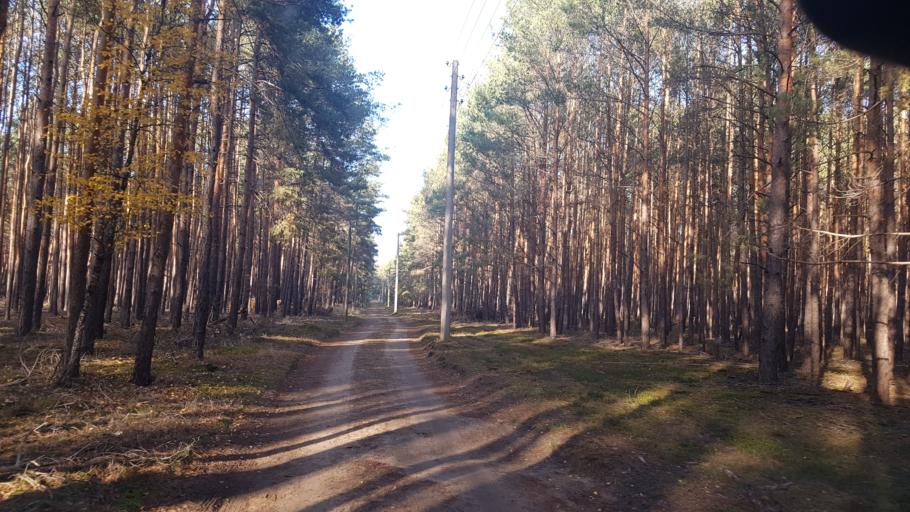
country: DE
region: Brandenburg
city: Schilda
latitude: 51.6420
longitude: 13.3507
